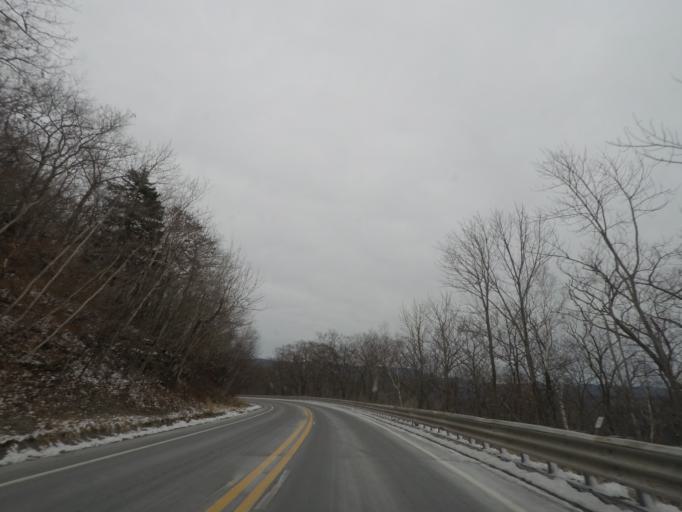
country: US
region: Massachusetts
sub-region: Berkshire County
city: Williamstown
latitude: 42.7198
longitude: -73.2648
